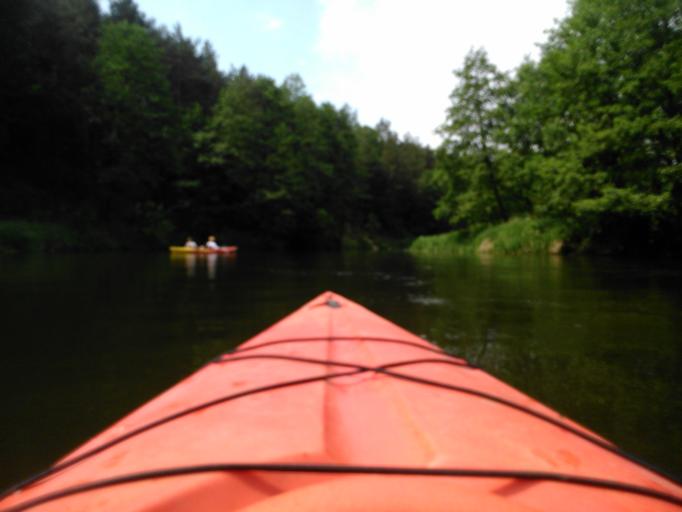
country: PL
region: Kujawsko-Pomorskie
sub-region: Powiat golubsko-dobrzynski
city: Golub-Dobrzyn
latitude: 53.1039
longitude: 19.0399
